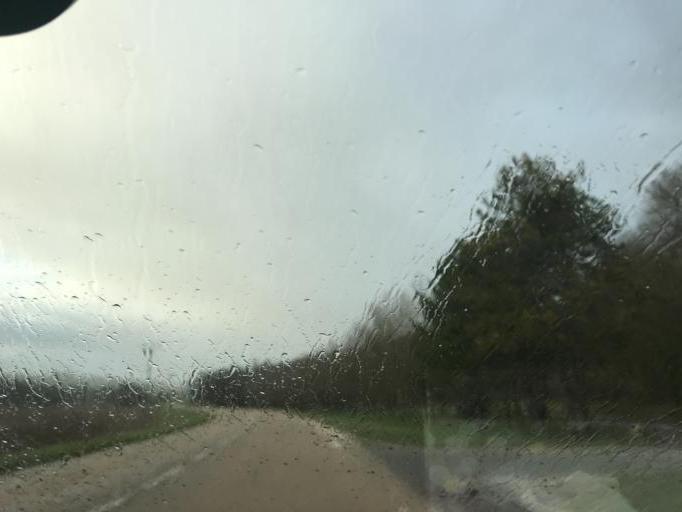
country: FR
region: Bourgogne
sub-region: Departement de l'Yonne
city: Fontenailles
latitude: 47.6204
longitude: 3.4965
